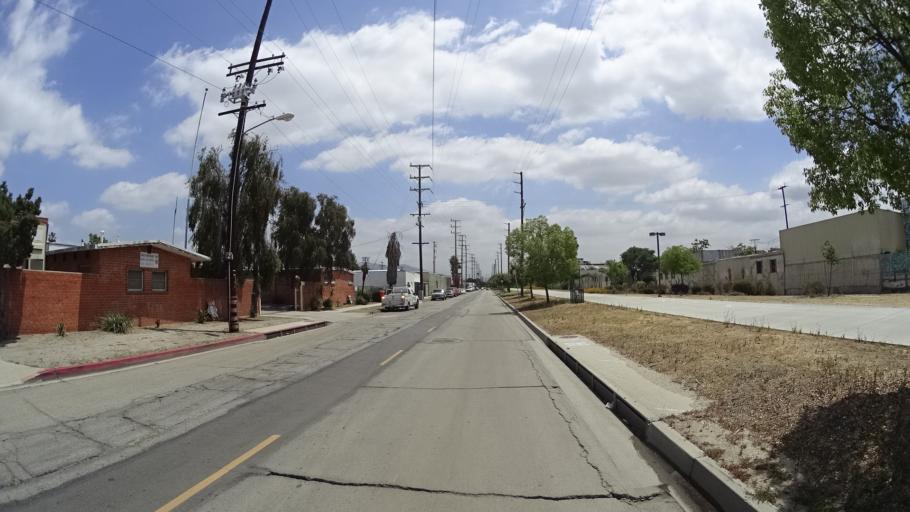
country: US
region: California
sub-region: Los Angeles County
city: North Hollywood
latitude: 34.1686
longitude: -118.3662
